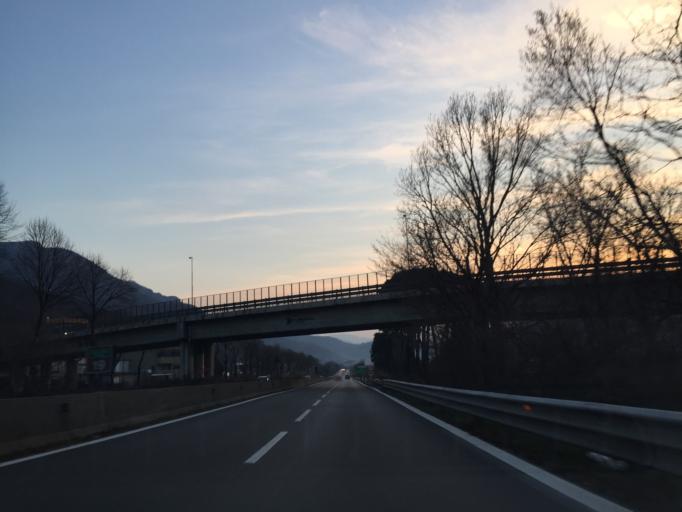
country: IT
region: Campania
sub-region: Provincia di Avellino
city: Solofra
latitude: 40.8315
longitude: 14.8195
